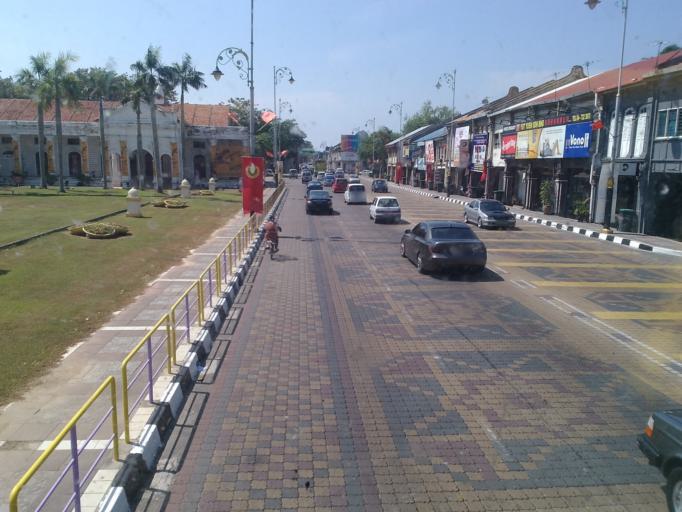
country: MY
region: Kedah
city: Alor Setar
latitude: 6.1196
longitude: 100.3656
